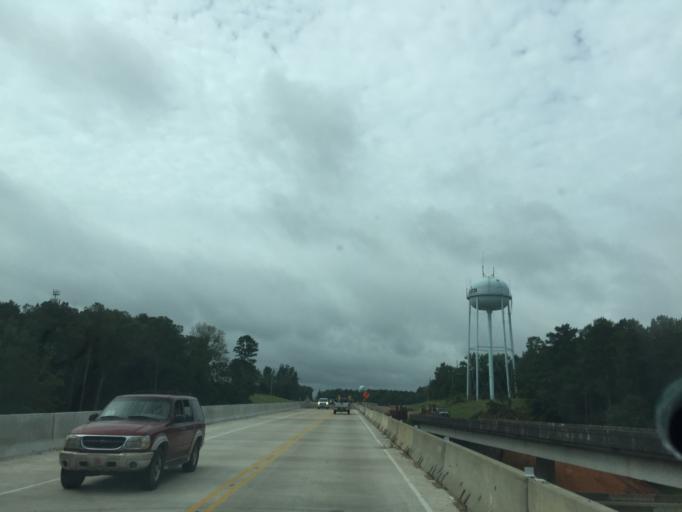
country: US
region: Mississippi
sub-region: Rankin County
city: Brandon
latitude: 32.2799
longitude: -89.9934
